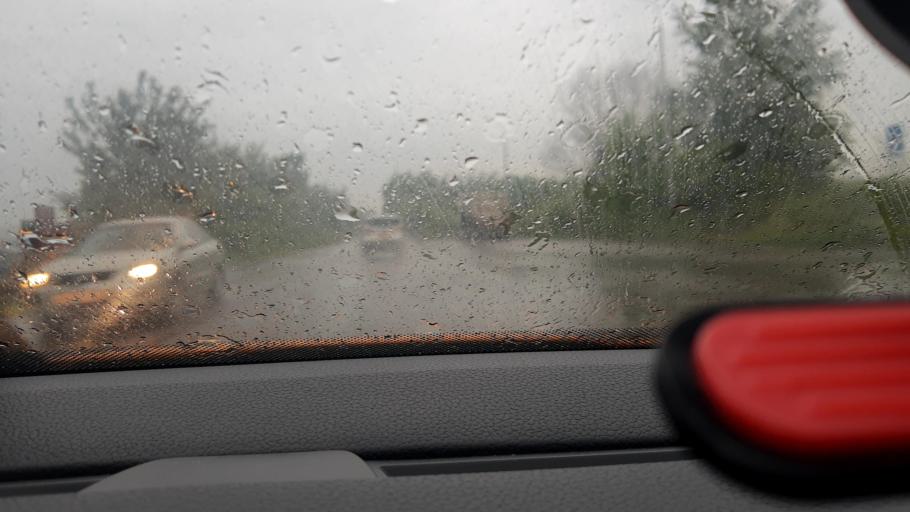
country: RU
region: Moskovskaya
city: Novopodrezkovo
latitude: 55.9371
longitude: 37.3781
